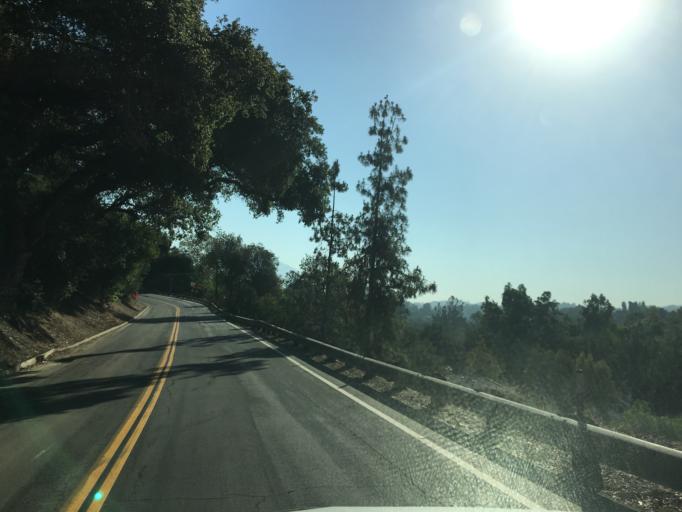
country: US
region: California
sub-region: Los Angeles County
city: Charter Oak
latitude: 34.0864
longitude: -117.8509
